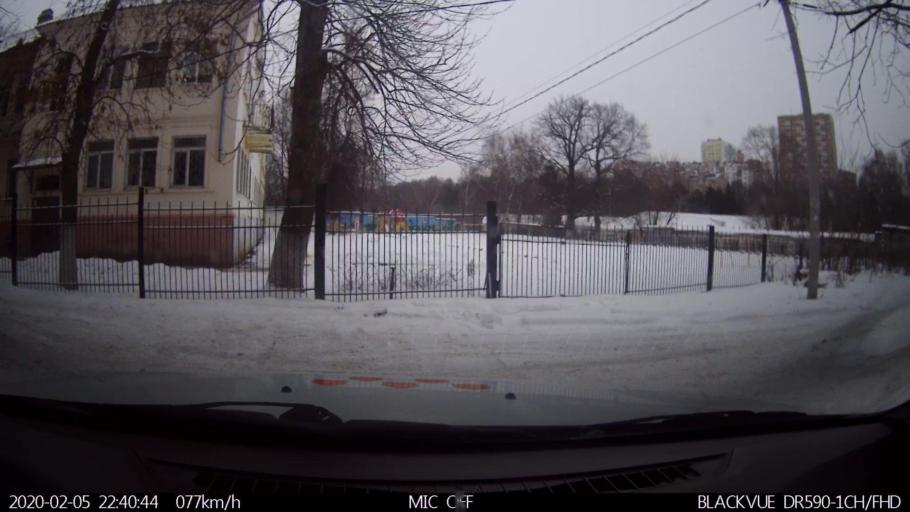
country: RU
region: Nizjnij Novgorod
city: Imeni Stepana Razina
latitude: 54.7229
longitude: 44.3263
